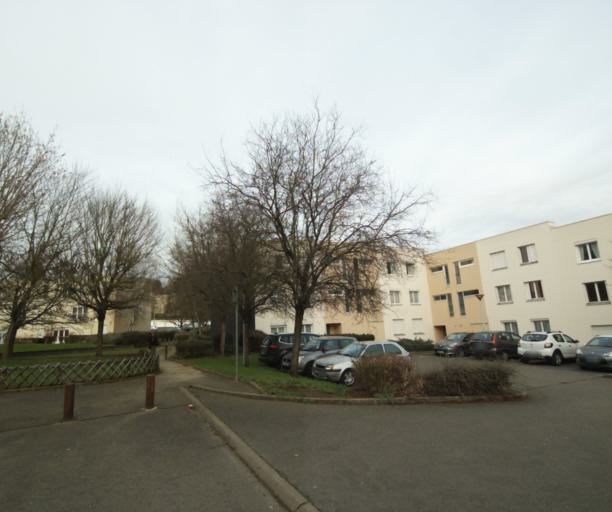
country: FR
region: Pays de la Loire
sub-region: Departement de la Sarthe
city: Le Mans
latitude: 48.0007
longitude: 0.2278
